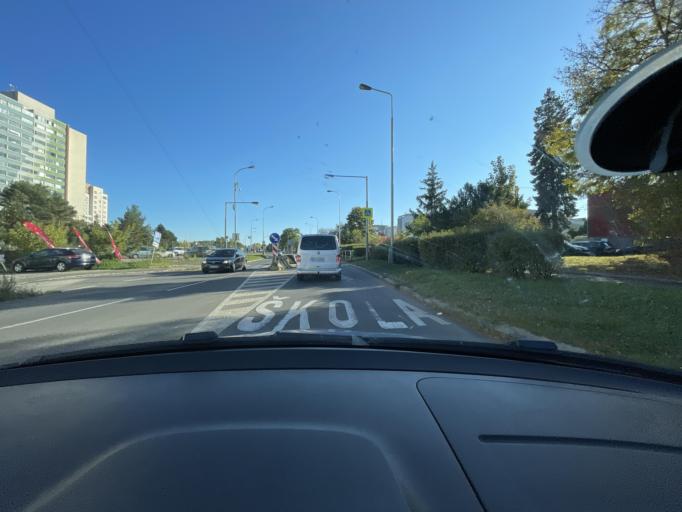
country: CZ
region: Praha
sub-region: Praha 4
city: Hodkovicky
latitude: 50.0211
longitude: 14.4515
